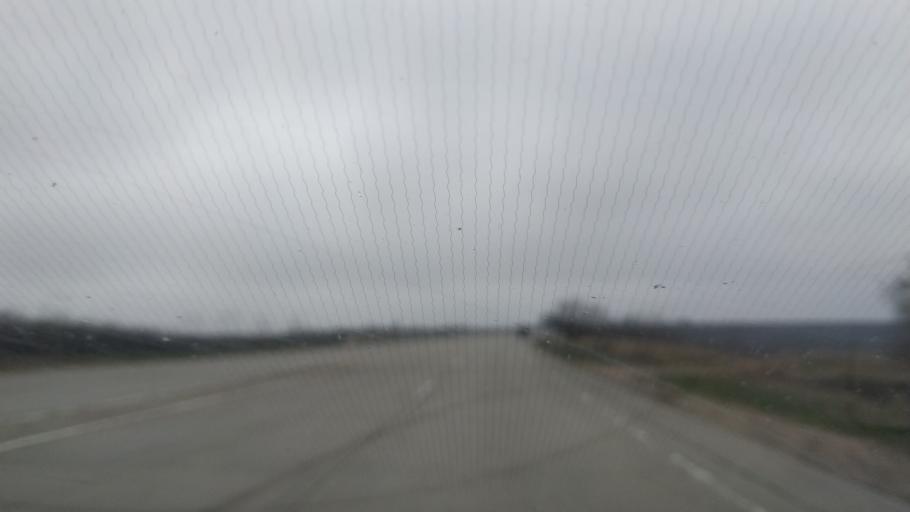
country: MD
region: Chisinau
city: Singera
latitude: 46.8737
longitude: 28.8814
